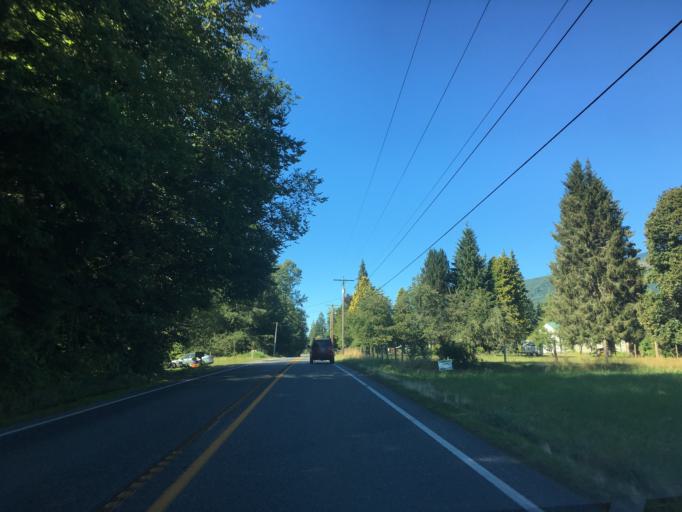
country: US
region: Washington
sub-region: Skagit County
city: Sedro-Woolley
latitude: 48.5465
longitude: -122.2255
